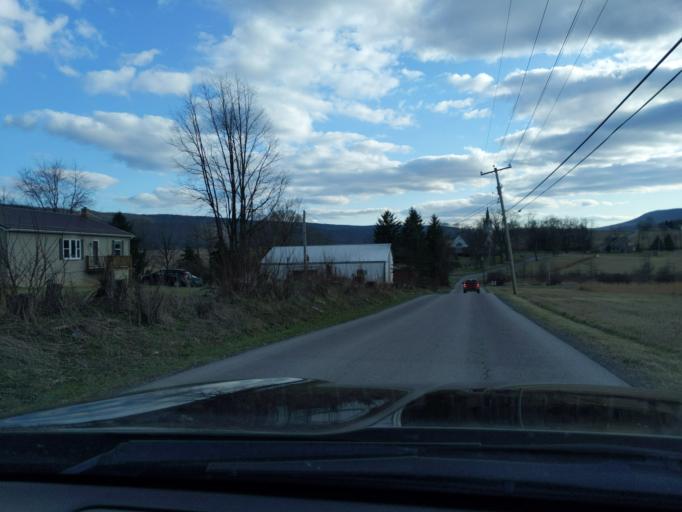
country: US
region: Pennsylvania
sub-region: Blair County
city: Tipton
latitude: 40.5969
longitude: -78.2489
